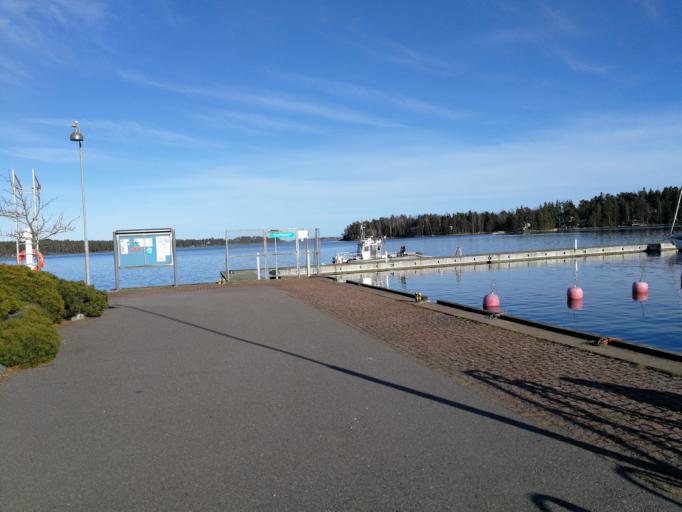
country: FI
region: Uusimaa
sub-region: Helsinki
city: Vantaa
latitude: 60.1989
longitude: 25.1409
